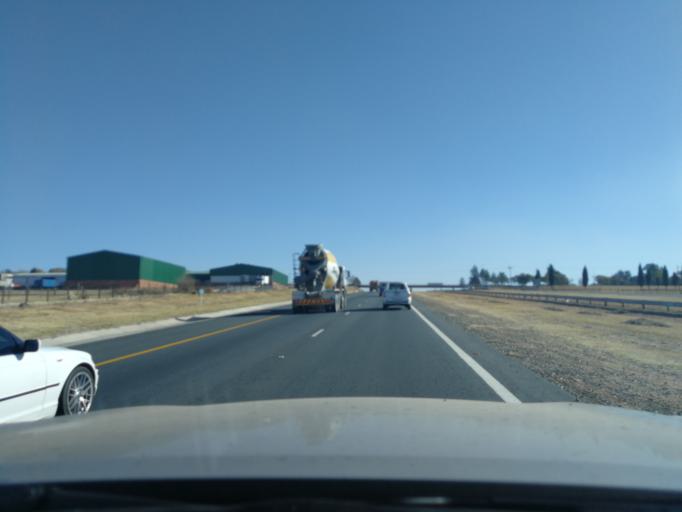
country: ZA
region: Gauteng
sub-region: West Rand District Municipality
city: Muldersdriseloop
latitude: -26.0110
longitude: 27.8846
